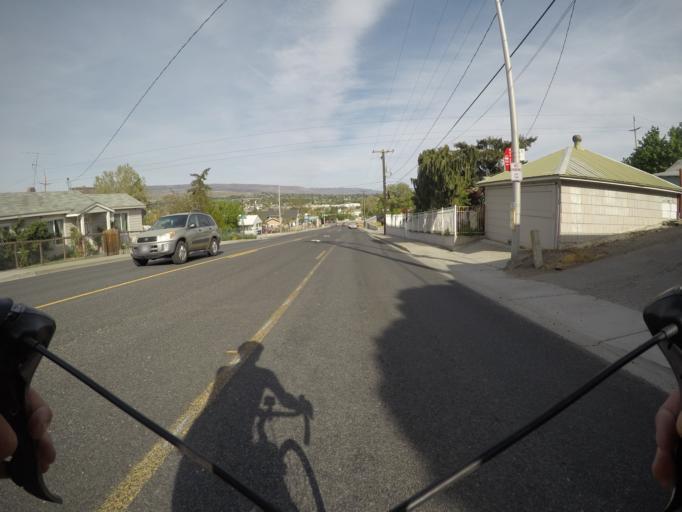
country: US
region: Washington
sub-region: Chelan County
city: Wenatchee
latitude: 47.4109
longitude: -120.3063
